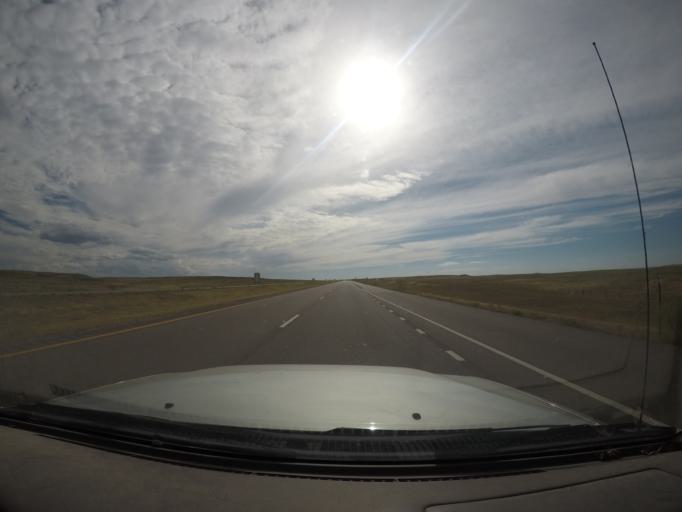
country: US
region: Nebraska
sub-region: Kimball County
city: Kimball
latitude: 41.2156
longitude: -103.6720
